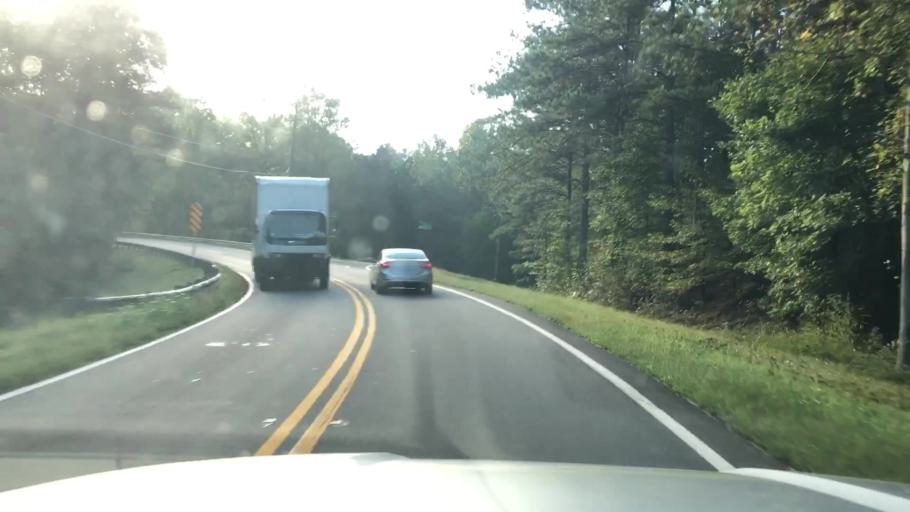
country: US
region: Georgia
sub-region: Bartow County
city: Emerson
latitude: 34.0791
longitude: -84.7558
